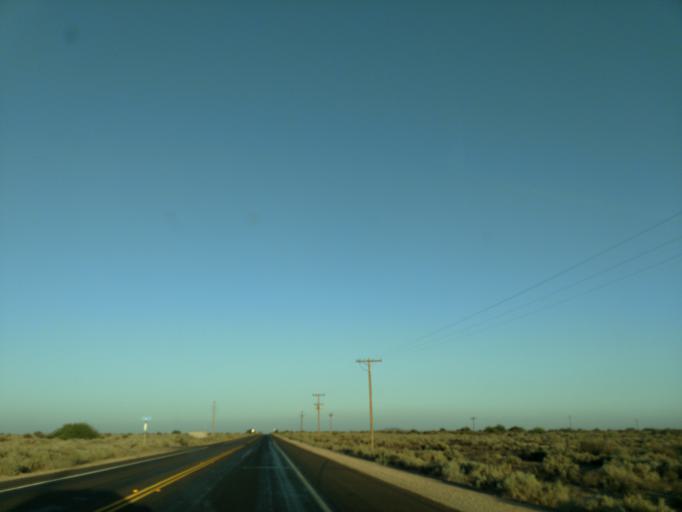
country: US
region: Arizona
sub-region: Maricopa County
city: Laveen
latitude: 33.2675
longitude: -112.1525
